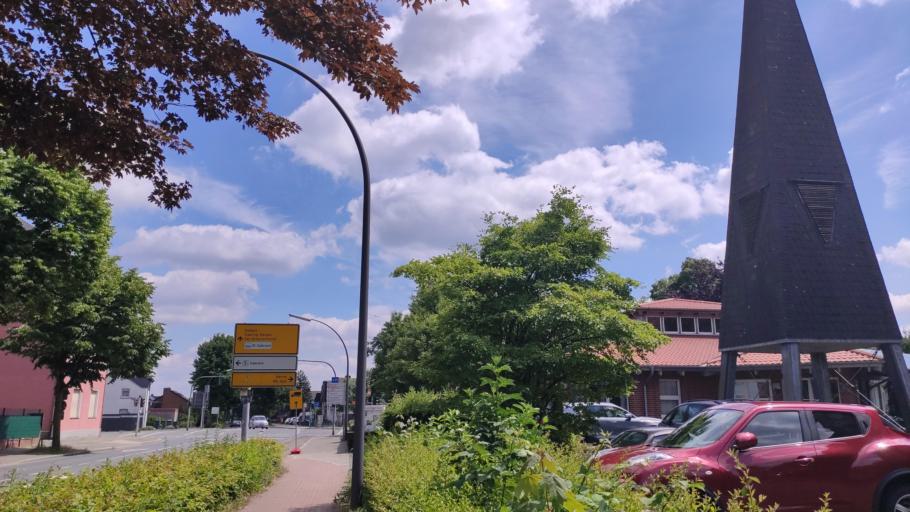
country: DE
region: North Rhine-Westphalia
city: Oer-Erkenschwick
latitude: 51.6019
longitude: 7.2620
